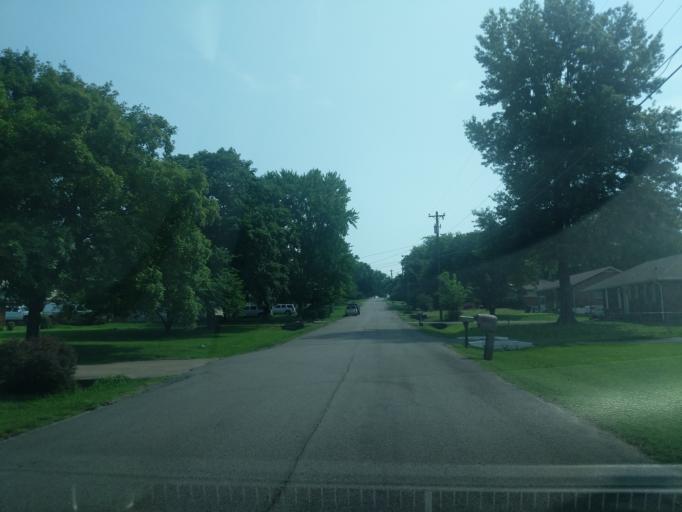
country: US
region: Tennessee
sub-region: Davidson County
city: Lakewood
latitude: 36.2628
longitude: -86.6665
